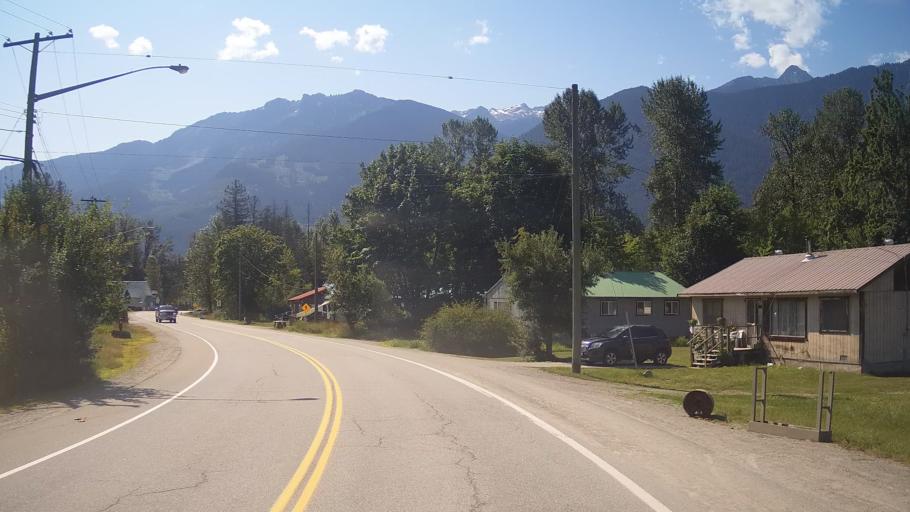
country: CA
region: British Columbia
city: Pemberton
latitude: 50.3179
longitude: -122.7196
